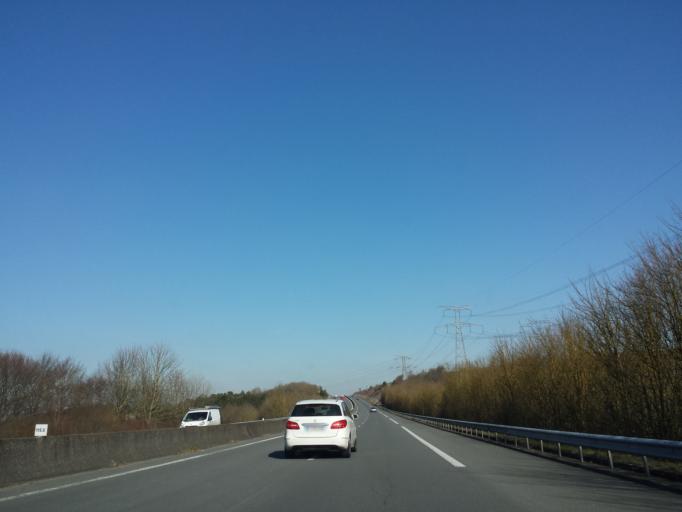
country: FR
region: Picardie
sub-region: Departement de la Somme
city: Saleux
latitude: 49.8025
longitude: 2.2420
